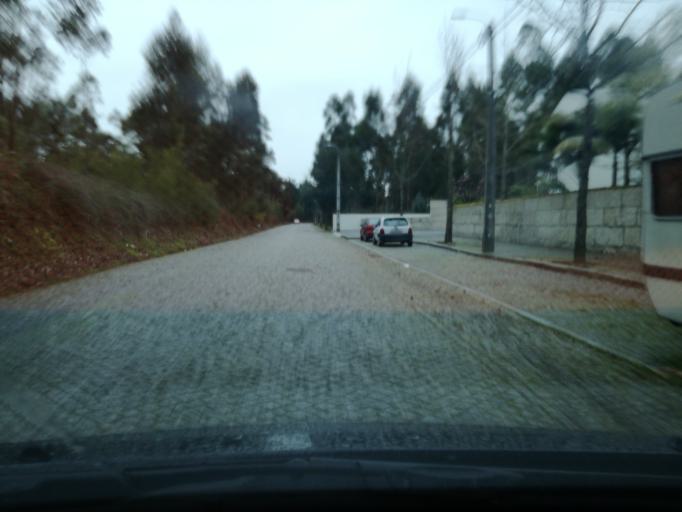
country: PT
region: Porto
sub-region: Maia
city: Gemunde
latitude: 41.2549
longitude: -8.6562
